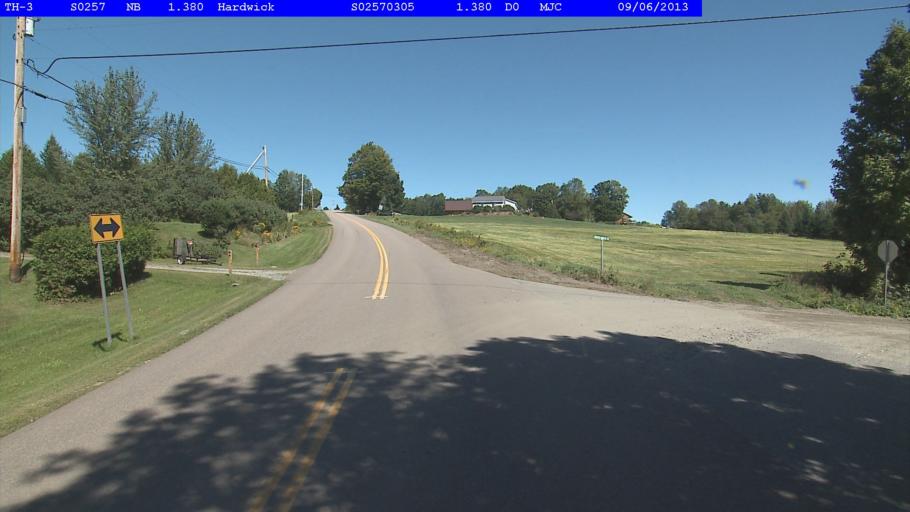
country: US
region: Vermont
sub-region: Caledonia County
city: Hardwick
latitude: 44.5111
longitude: -72.3431
